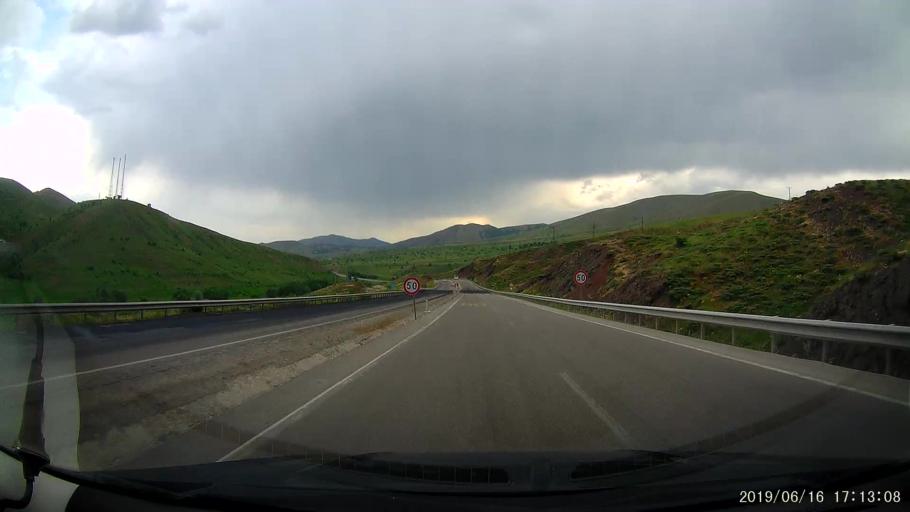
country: TR
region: Erzurum
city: Askale
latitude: 39.8599
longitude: 40.6051
